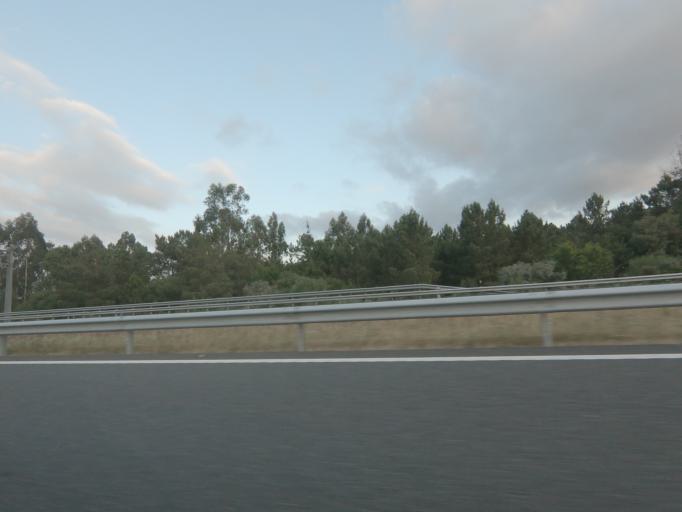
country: ES
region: Galicia
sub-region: Provincia de Pontevedra
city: Covelo
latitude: 42.2015
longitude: -8.2827
